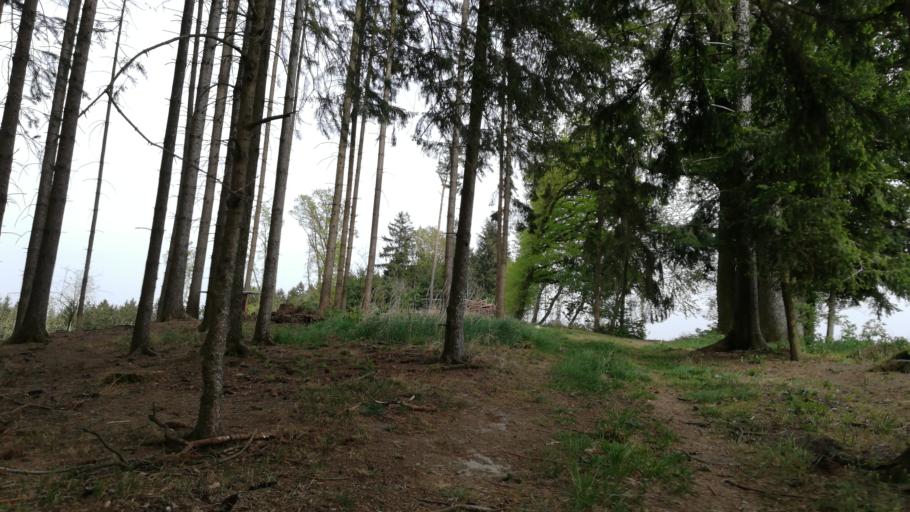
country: AT
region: Upper Austria
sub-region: Politischer Bezirk Grieskirchen
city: Bad Schallerbach
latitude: 48.1860
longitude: 13.9327
